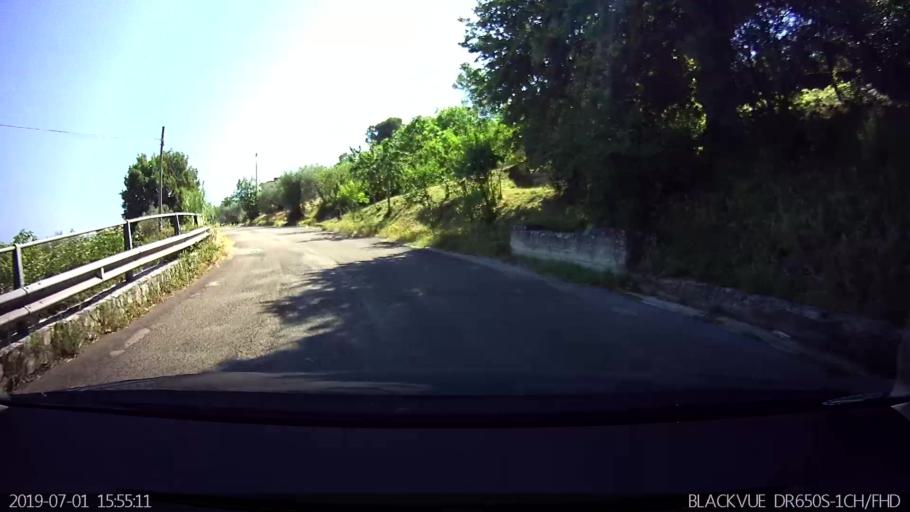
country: IT
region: Latium
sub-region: Provincia di Frosinone
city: Veroli
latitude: 41.6899
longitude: 13.4224
